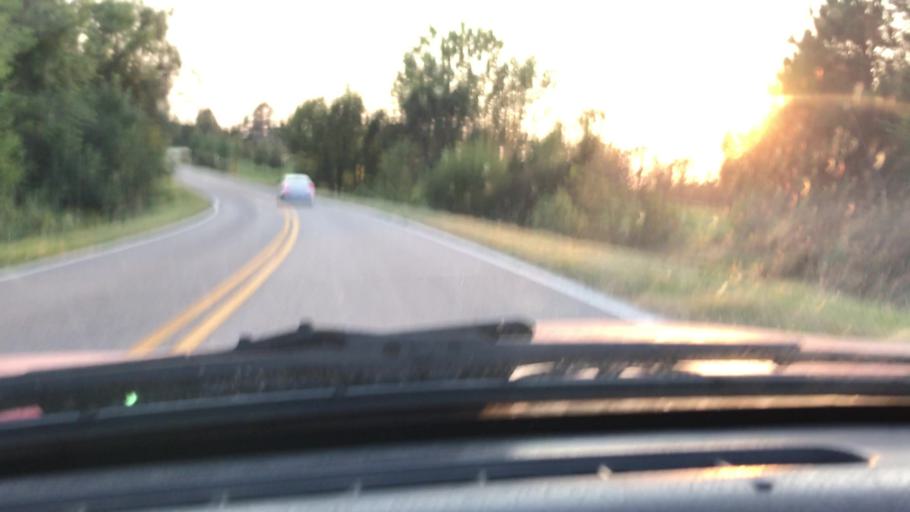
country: US
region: Nebraska
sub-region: Lancaster County
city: Lincoln
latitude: 40.7701
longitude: -96.7356
